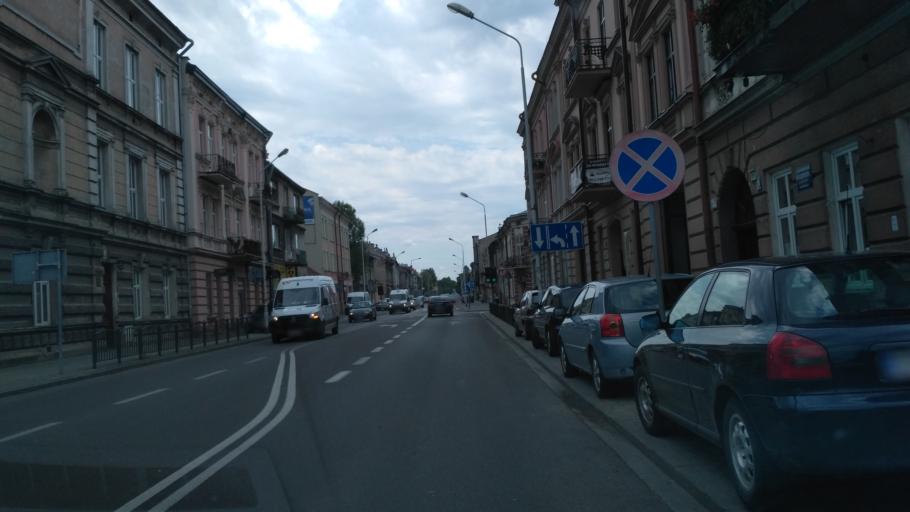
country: PL
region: Subcarpathian Voivodeship
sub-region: Przemysl
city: Przemysl
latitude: 49.7863
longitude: 22.7627
